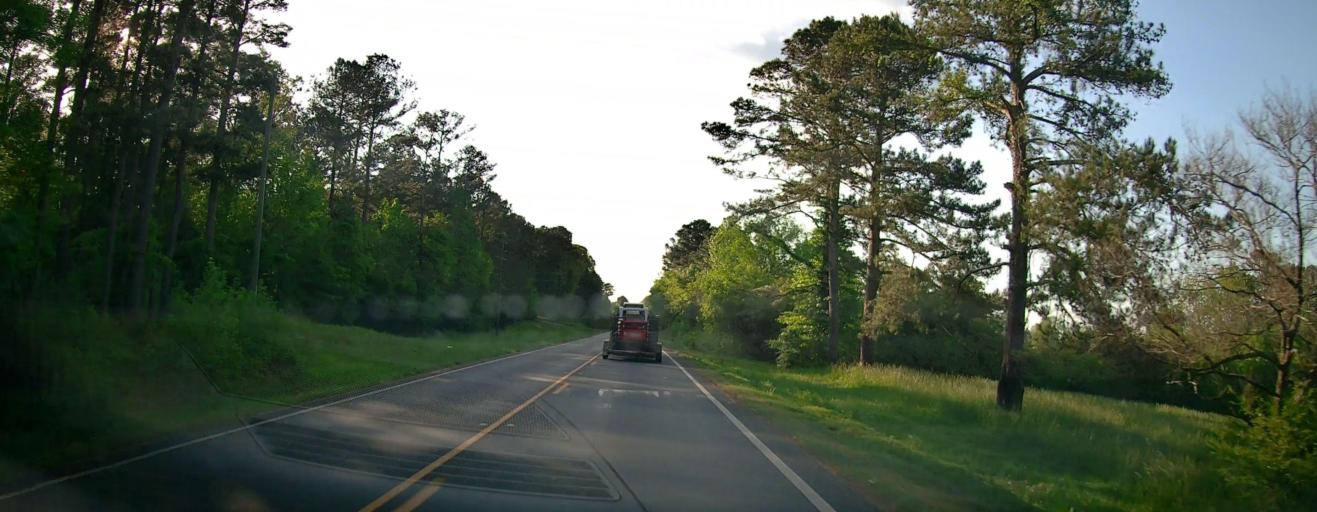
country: US
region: Georgia
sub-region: Putnam County
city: Eatonton
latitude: 33.3262
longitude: -83.4991
